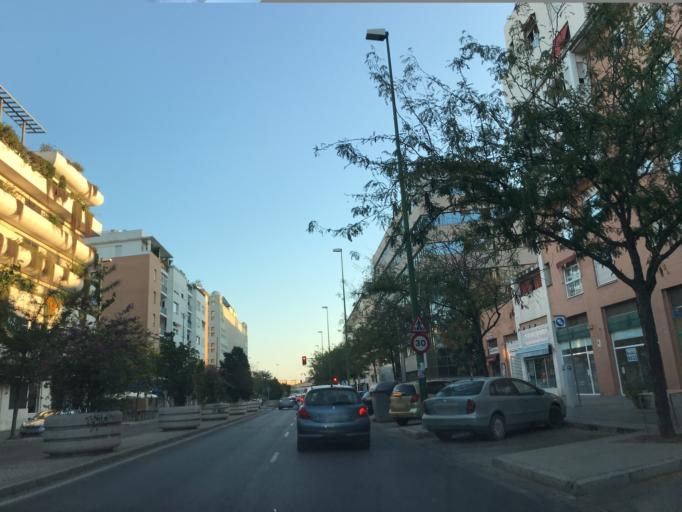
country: ES
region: Andalusia
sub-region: Provincia de Sevilla
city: Sevilla
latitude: 37.3852
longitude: -5.9788
